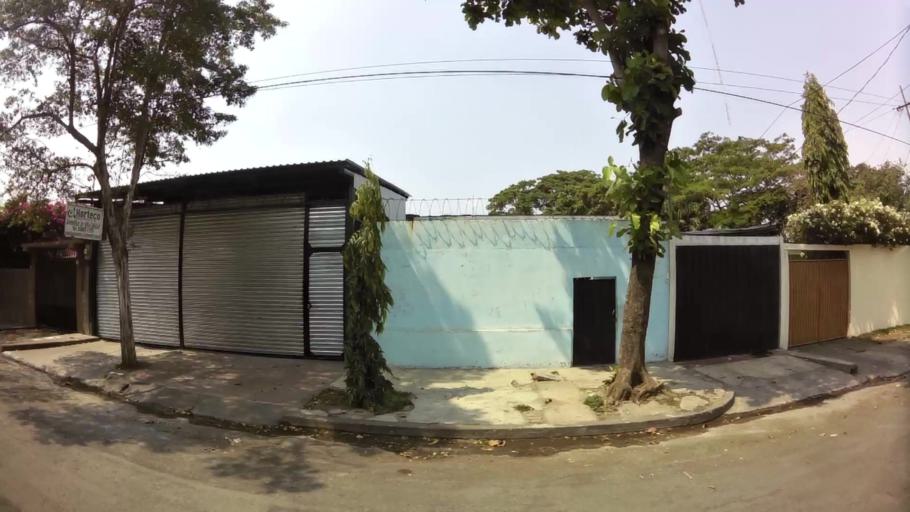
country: NI
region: Managua
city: Ciudad Sandino
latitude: 12.1267
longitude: -86.3134
